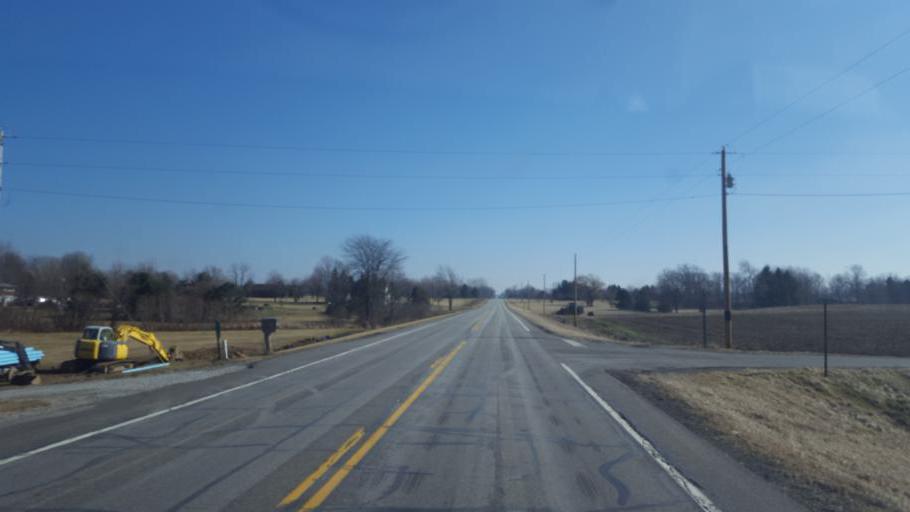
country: US
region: Ohio
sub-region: Huron County
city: Plymouth
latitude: 41.0314
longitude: -82.6525
